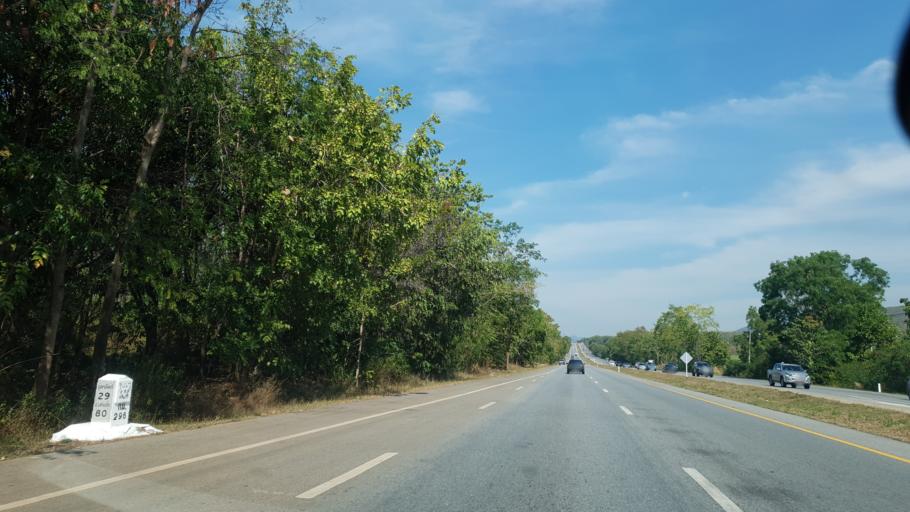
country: TH
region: Uttaradit
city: Thong Saen Khan
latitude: 17.4344
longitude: 100.2289
